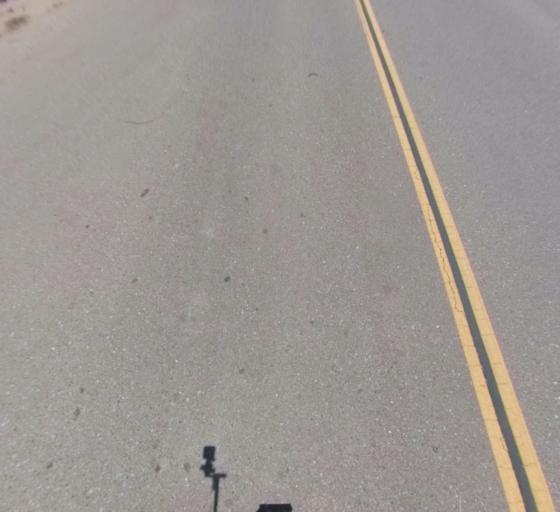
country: US
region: California
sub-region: Madera County
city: Parkwood
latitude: 36.8731
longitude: -120.0558
